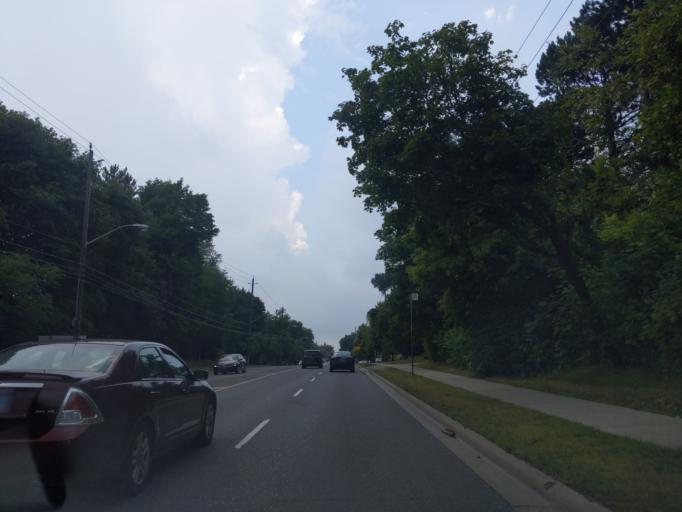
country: CA
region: Ontario
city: Willowdale
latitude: 43.8030
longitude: -79.3981
